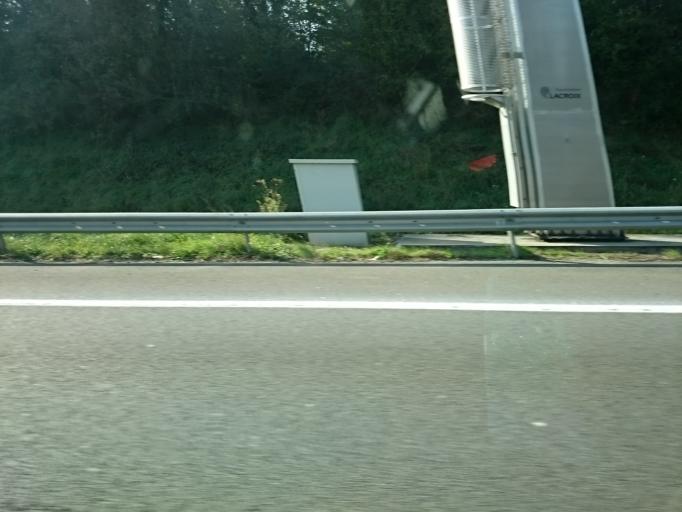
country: FR
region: Pays de la Loire
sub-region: Departement de la Loire-Atlantique
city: Orvault
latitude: 47.2462
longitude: -1.6216
